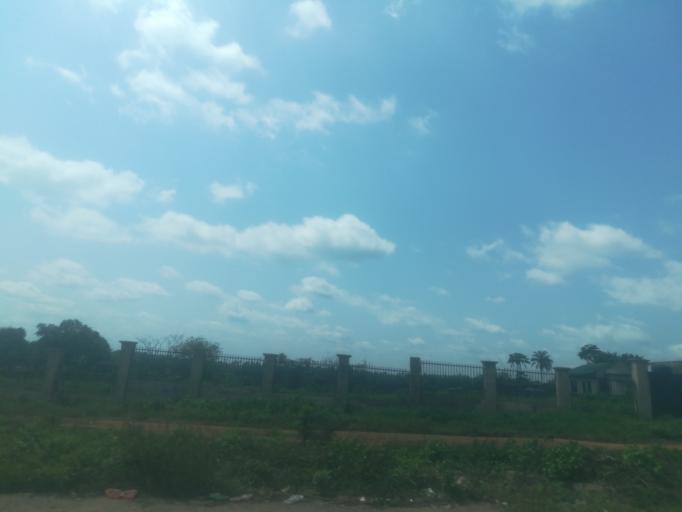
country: NG
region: Oyo
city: Moniya
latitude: 7.5805
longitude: 3.9149
